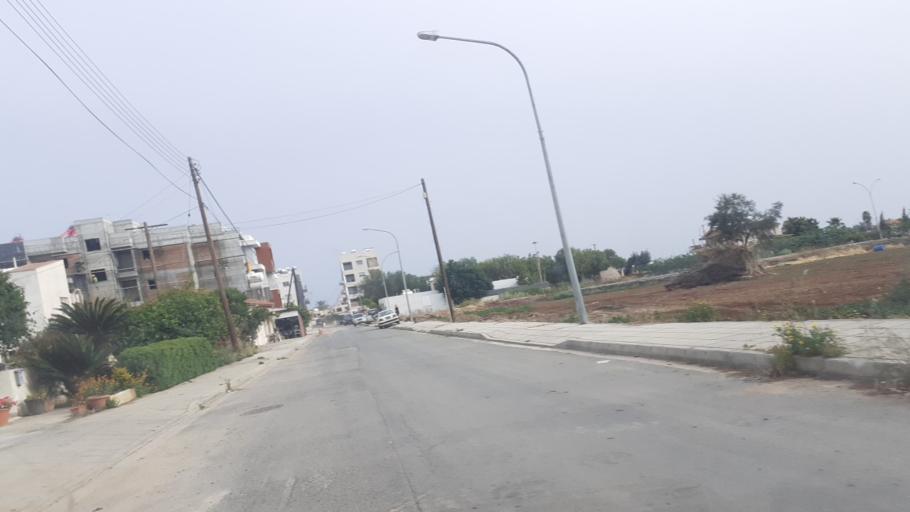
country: CY
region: Limassol
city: Limassol
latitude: 34.6519
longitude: 33.0036
